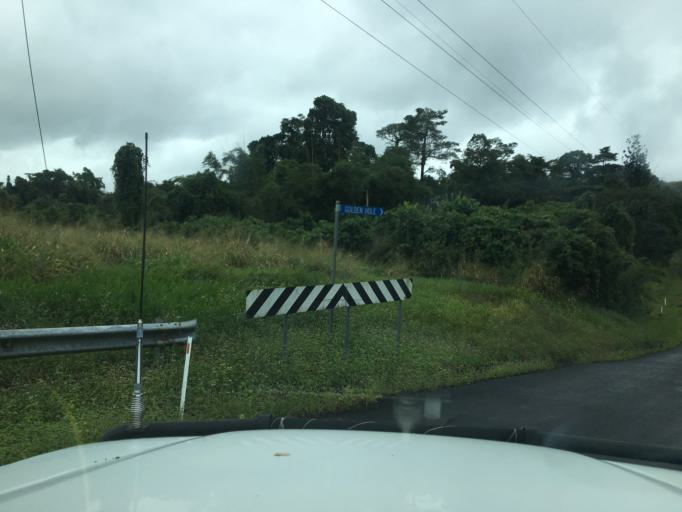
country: AU
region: Queensland
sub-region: Cassowary Coast
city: Innisfail
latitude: -17.4432
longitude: 145.8608
